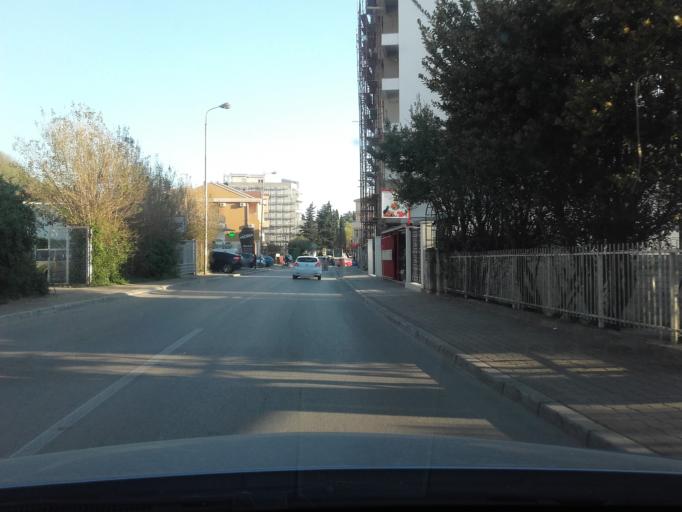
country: ME
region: Budva
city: Budva
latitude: 42.2886
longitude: 18.8518
